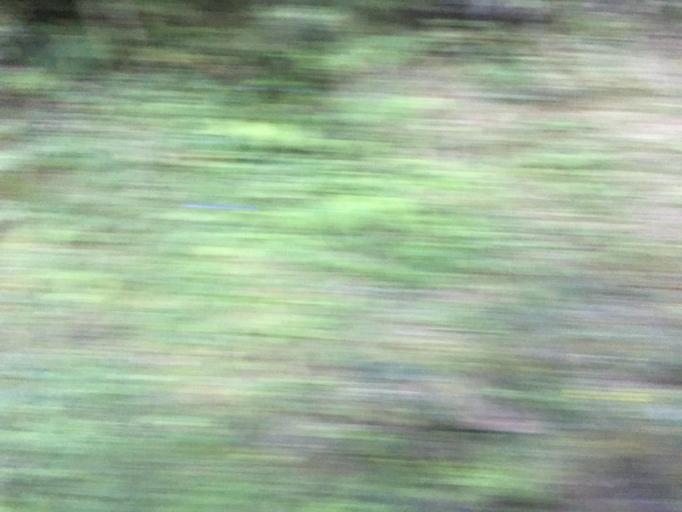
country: TW
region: Taiwan
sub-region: Yilan
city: Yilan
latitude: 24.5338
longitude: 121.5168
